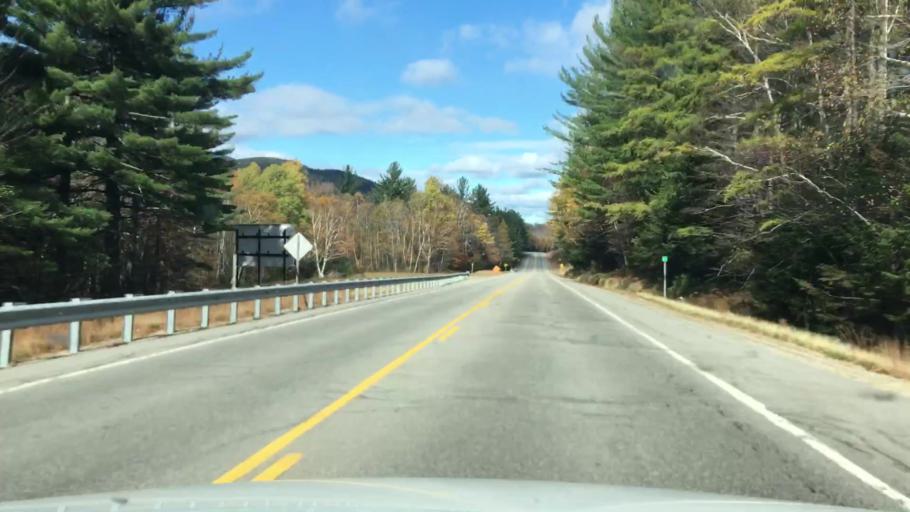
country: US
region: New Hampshire
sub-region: Coos County
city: Gorham
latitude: 44.2924
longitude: -71.2243
